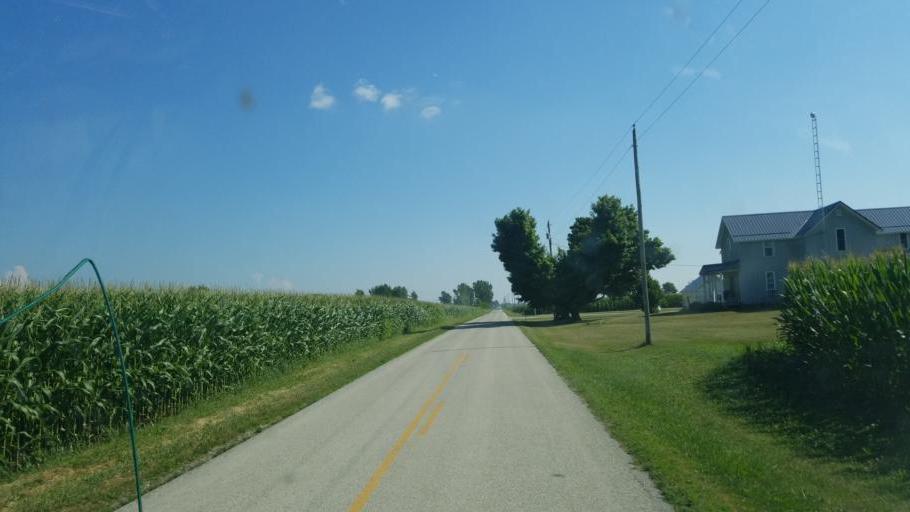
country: US
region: Ohio
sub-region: Hardin County
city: Kenton
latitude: 40.6863
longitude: -83.5144
